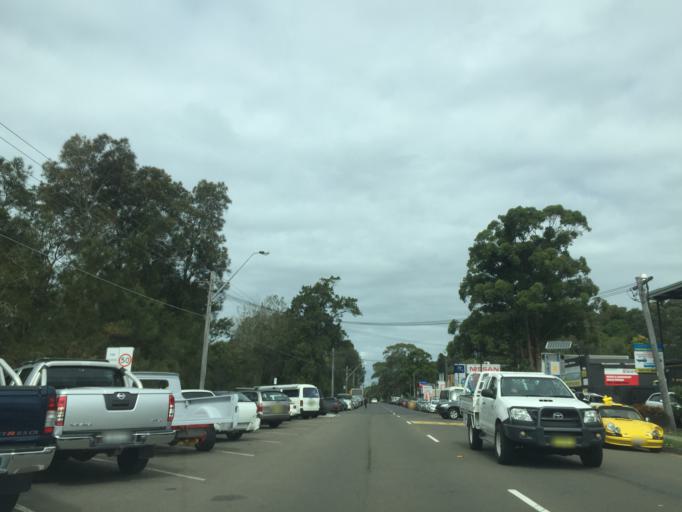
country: AU
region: New South Wales
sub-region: Pittwater
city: North Narrabeen
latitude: -33.7005
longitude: 151.2950
